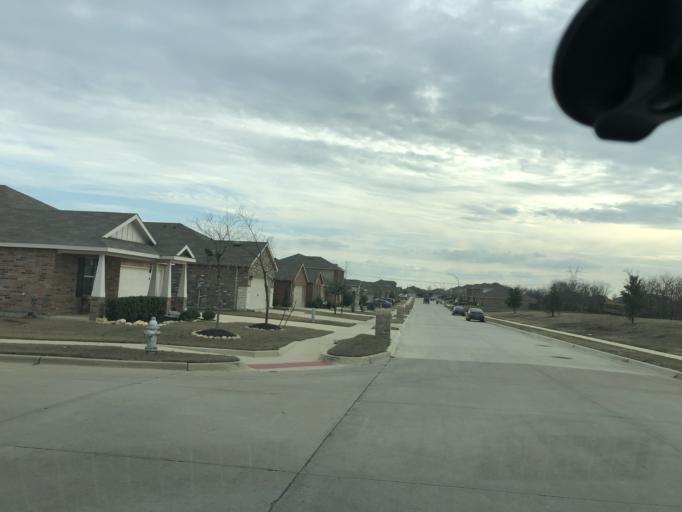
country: US
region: Texas
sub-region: Tarrant County
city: Saginaw
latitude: 32.9133
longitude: -97.3679
